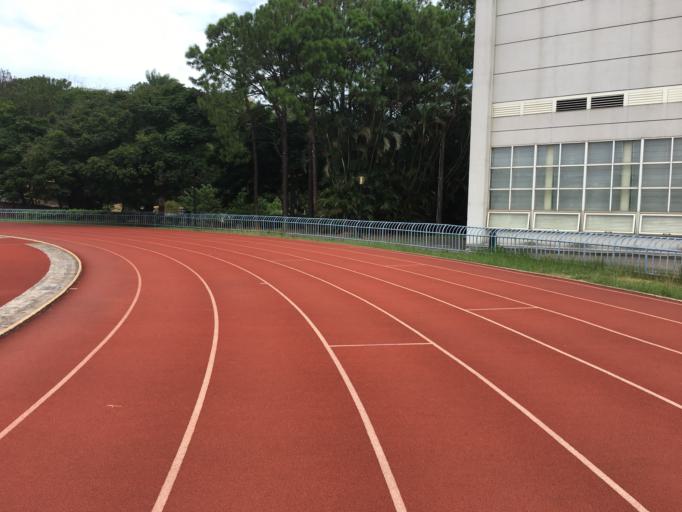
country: TW
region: Taiwan
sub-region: Hsinchu
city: Hsinchu
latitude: 24.7895
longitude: 120.9949
